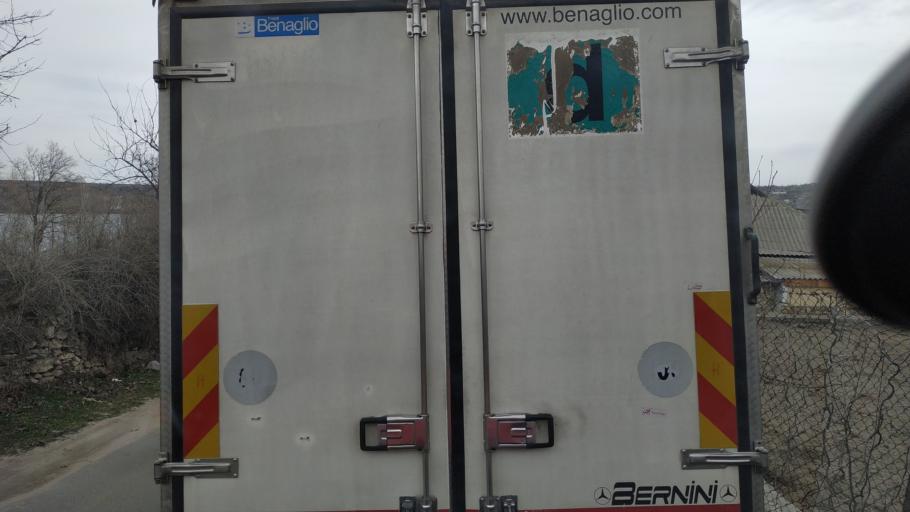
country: MD
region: Telenesti
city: Cocieri
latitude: 47.3493
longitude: 29.0919
